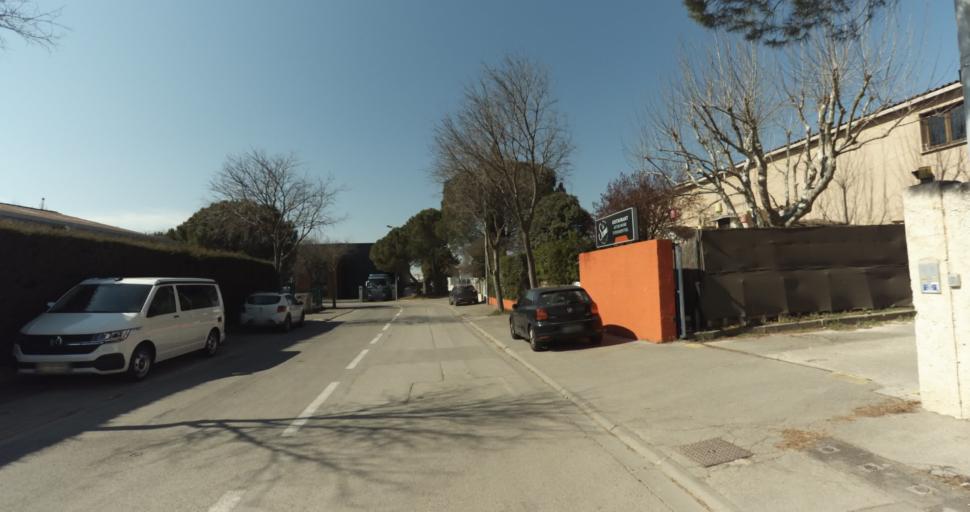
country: FR
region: Provence-Alpes-Cote d'Azur
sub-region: Departement des Bouches-du-Rhone
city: Cabries
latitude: 43.4815
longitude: 5.3832
